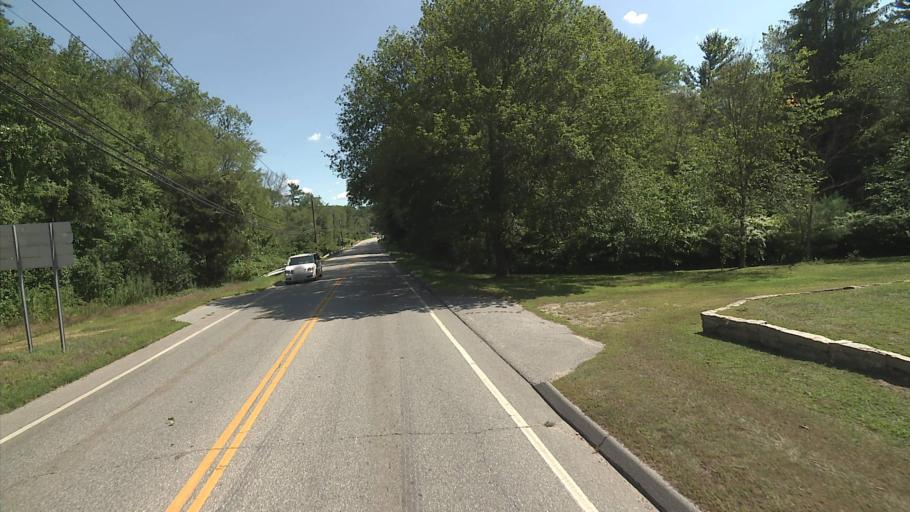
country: US
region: Connecticut
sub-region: Windham County
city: Plainfield
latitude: 41.5751
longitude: -71.8604
